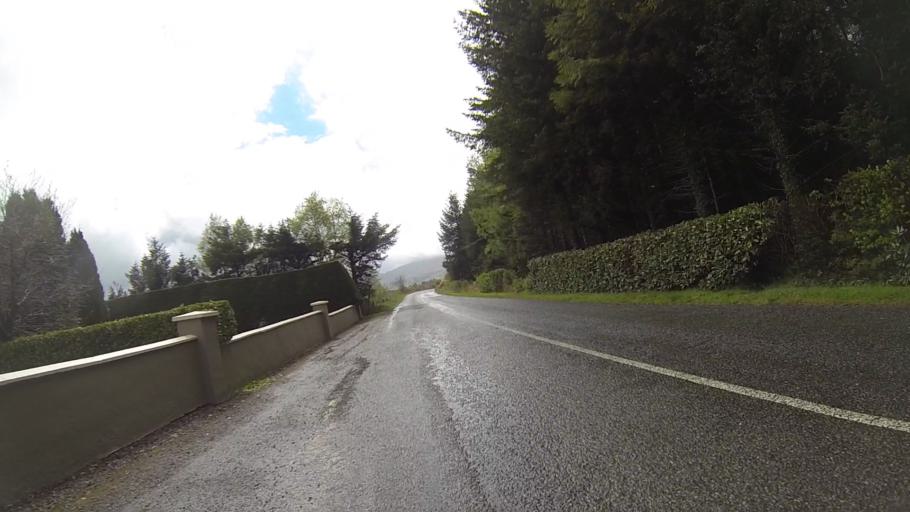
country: IE
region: Munster
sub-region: Ciarrai
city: Kenmare
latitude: 51.9032
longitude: -9.7424
